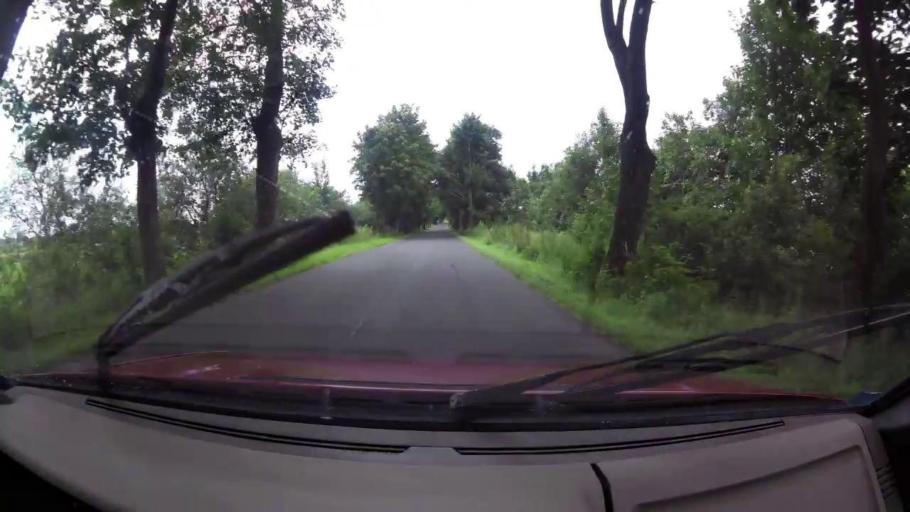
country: PL
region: West Pomeranian Voivodeship
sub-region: Koszalin
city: Koszalin
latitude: 54.1510
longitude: 16.1319
